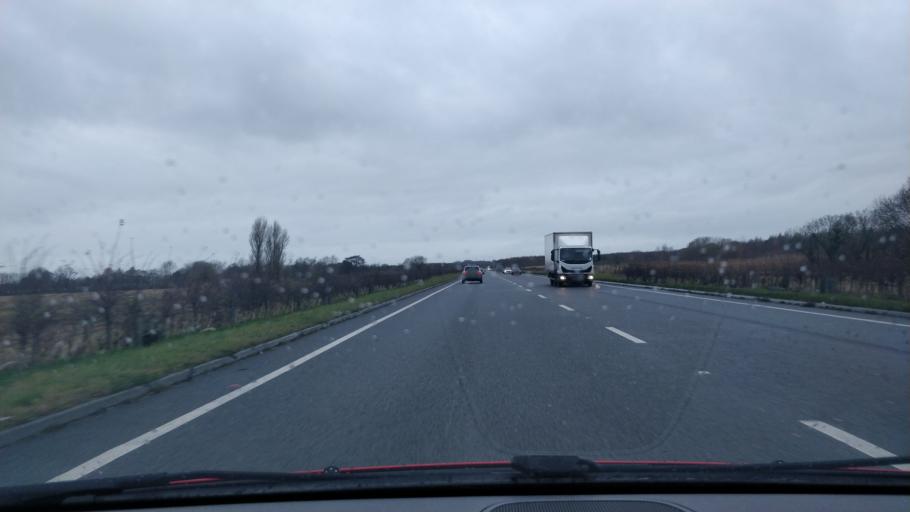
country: GB
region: England
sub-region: Sefton
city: Thornton
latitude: 53.5000
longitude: -2.9851
